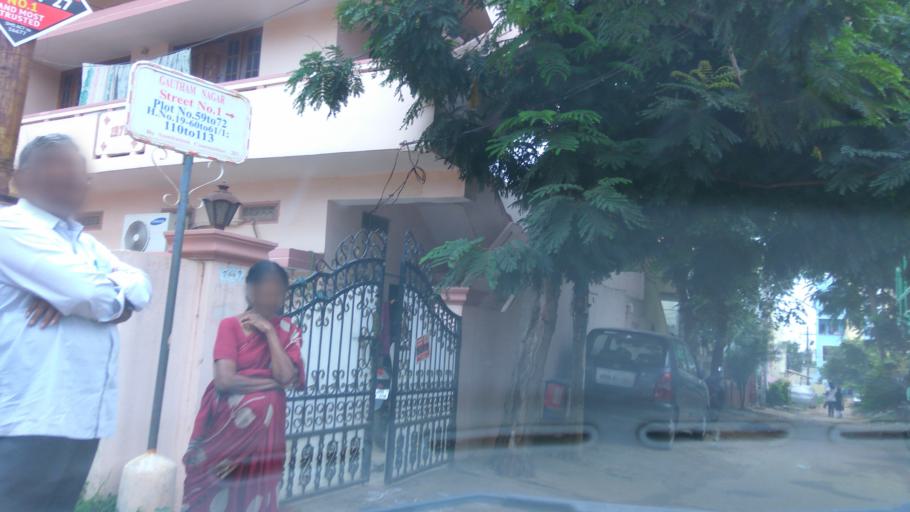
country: IN
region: Telangana
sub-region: Hyderabad
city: Malkajgiri
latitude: 17.4552
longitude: 78.5297
